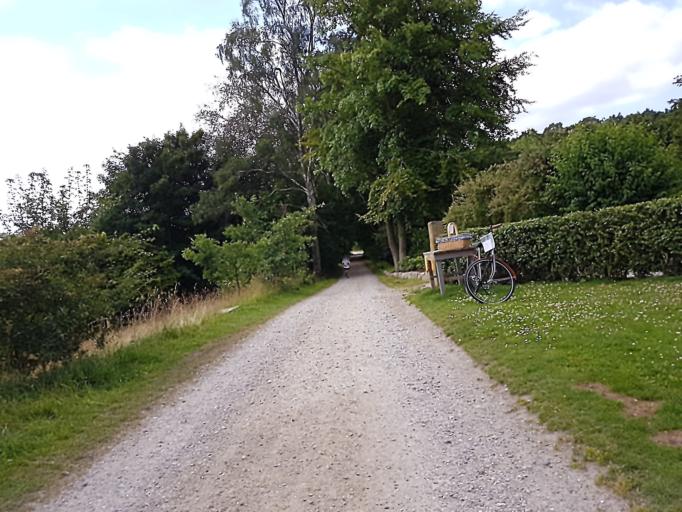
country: DK
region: Capital Region
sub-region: Fureso Kommune
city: Farum
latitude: 55.7972
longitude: 12.3345
